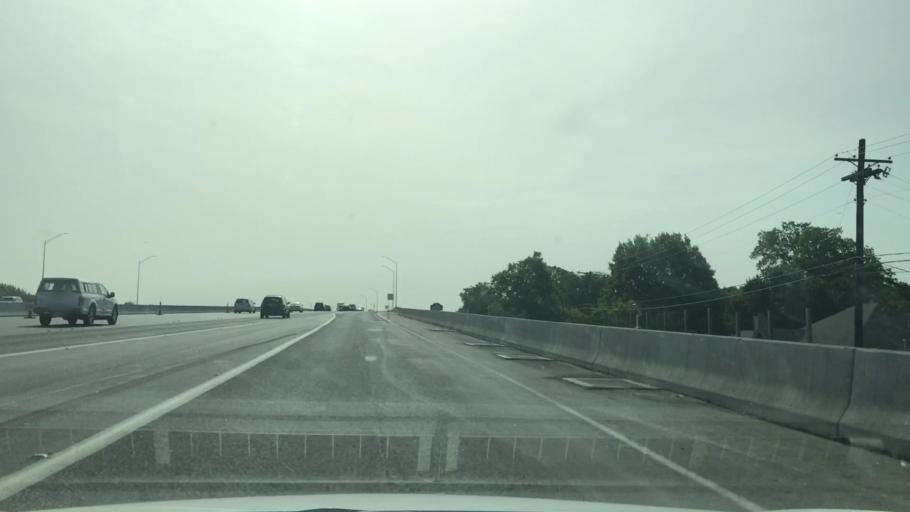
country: US
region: Texas
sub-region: Tarrant County
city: Euless
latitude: 32.8373
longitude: -97.0945
